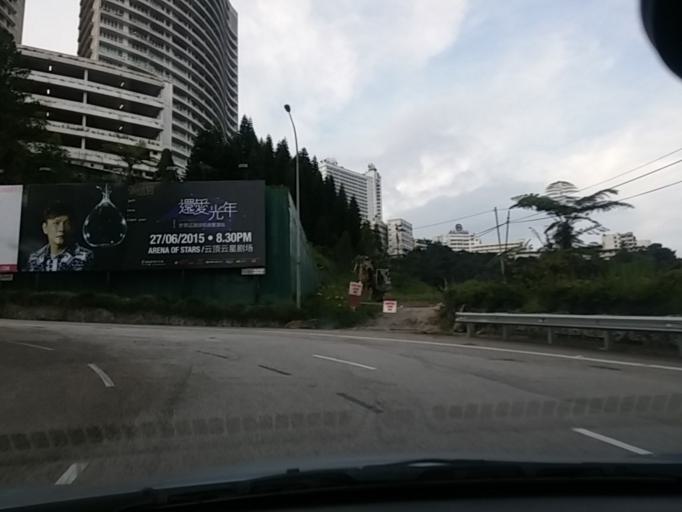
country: MY
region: Pahang
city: Kampung Bukit Tinggi, Bentong
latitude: 3.4184
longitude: 101.7898
